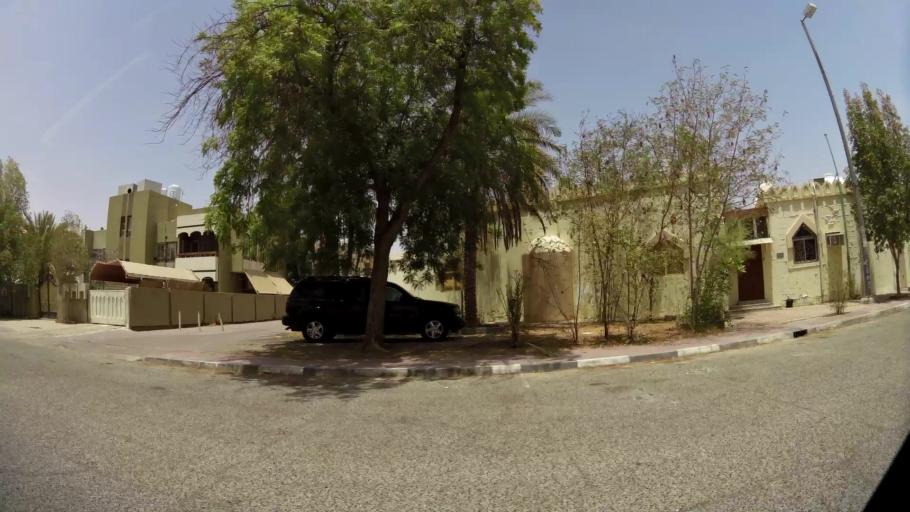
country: AE
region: Abu Dhabi
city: Al Ain
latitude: 24.2052
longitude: 55.7137
